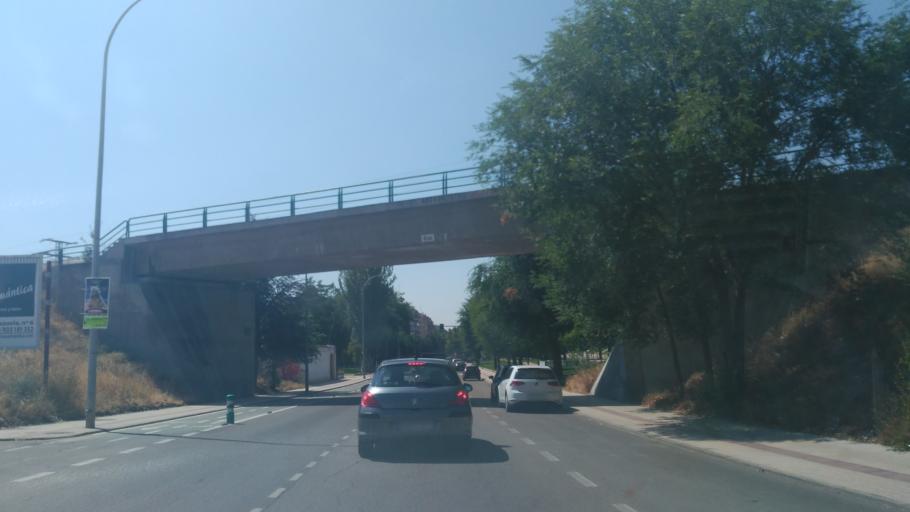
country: ES
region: Castille and Leon
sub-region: Provincia de Salamanca
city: Salamanca
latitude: 40.9821
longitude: -5.6502
